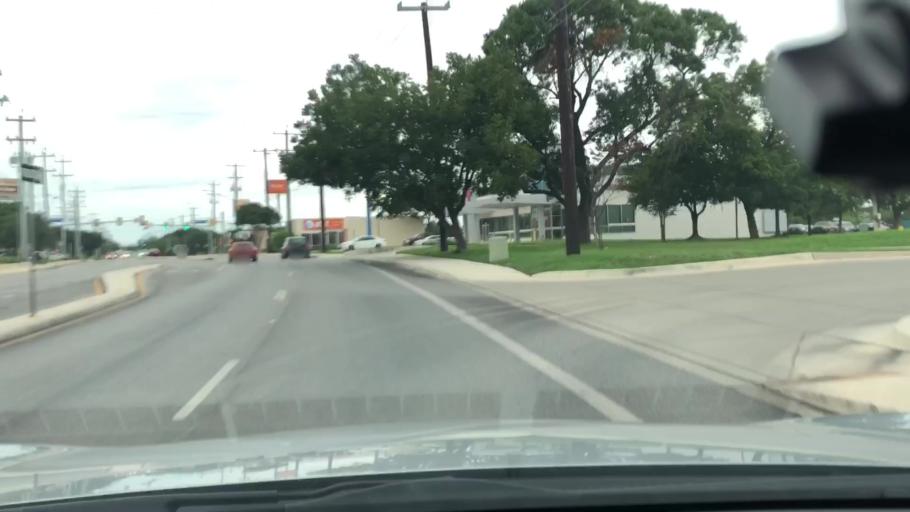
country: US
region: Texas
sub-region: Bexar County
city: Leon Valley
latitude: 29.4852
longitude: -98.6659
